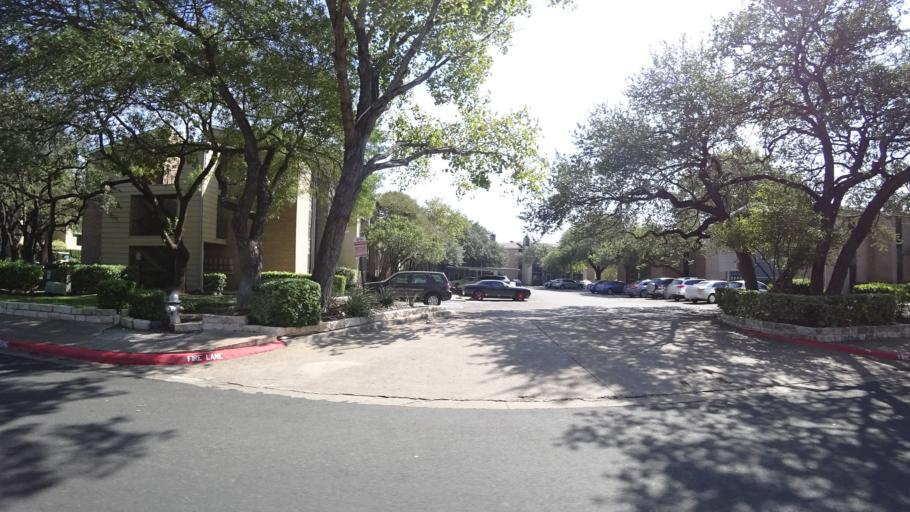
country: US
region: Texas
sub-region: Travis County
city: West Lake Hills
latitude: 30.3504
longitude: -97.7551
